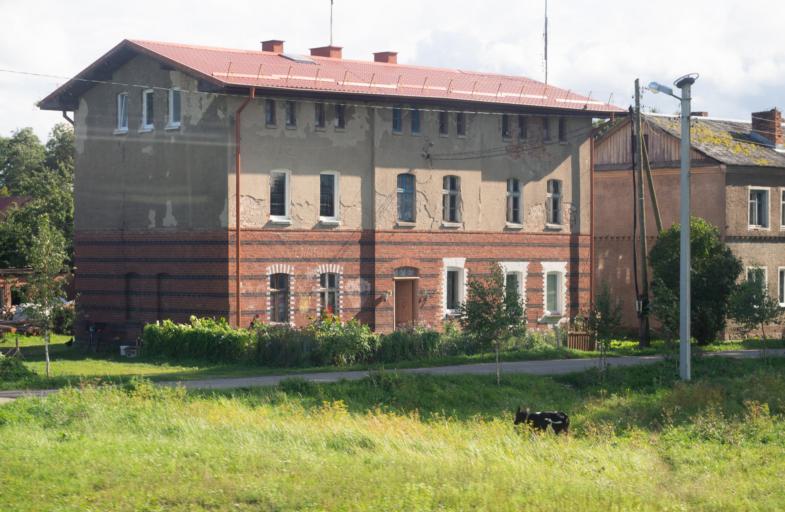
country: RU
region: Kaliningrad
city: Zheleznodorozhnyy
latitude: 54.4461
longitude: 21.4761
